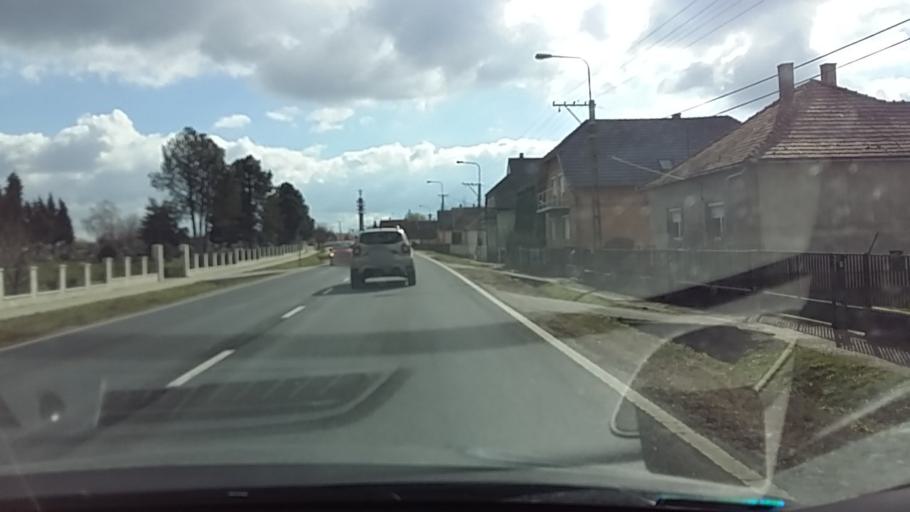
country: HU
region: Somogy
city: Nagybajom
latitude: 46.3961
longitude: 17.4963
